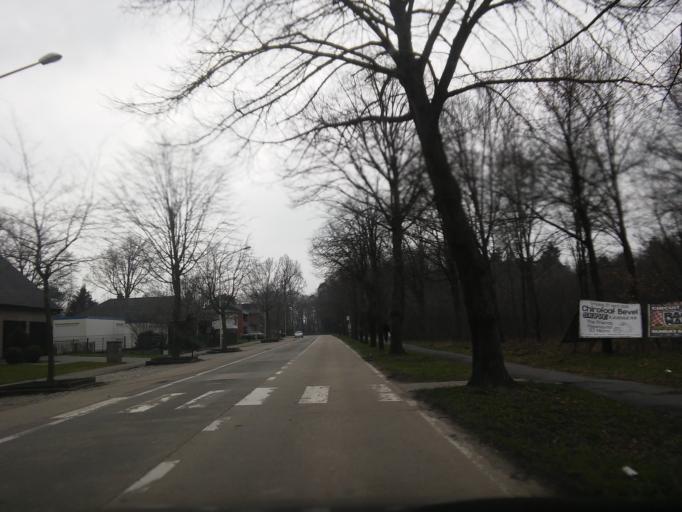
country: BE
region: Flanders
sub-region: Provincie Antwerpen
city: Grobbendonk
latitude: 51.1698
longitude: 4.7448
